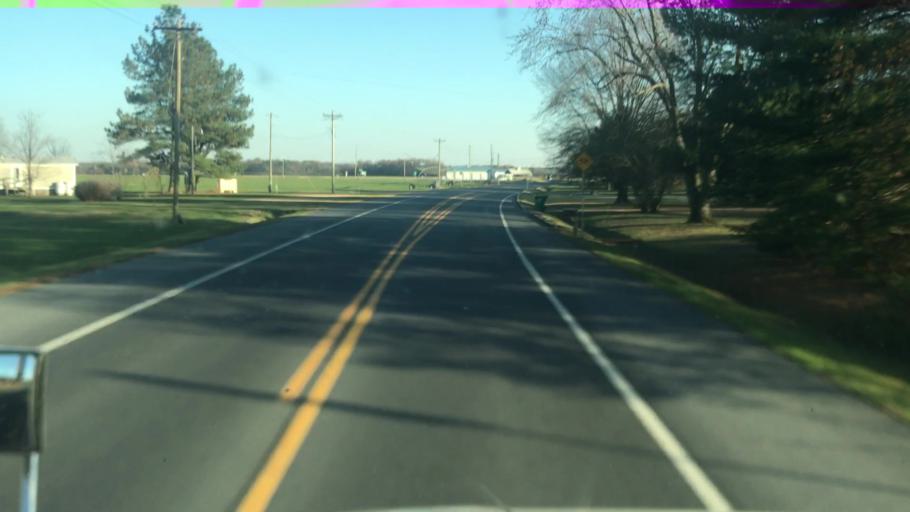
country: US
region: Delaware
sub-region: Sussex County
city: Bridgeville
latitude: 38.7820
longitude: -75.6700
